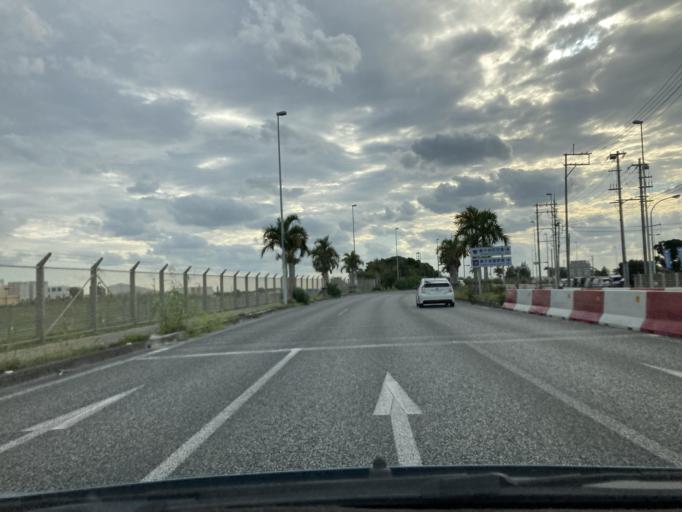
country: JP
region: Okinawa
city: Okinawa
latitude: 26.3604
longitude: 127.7548
